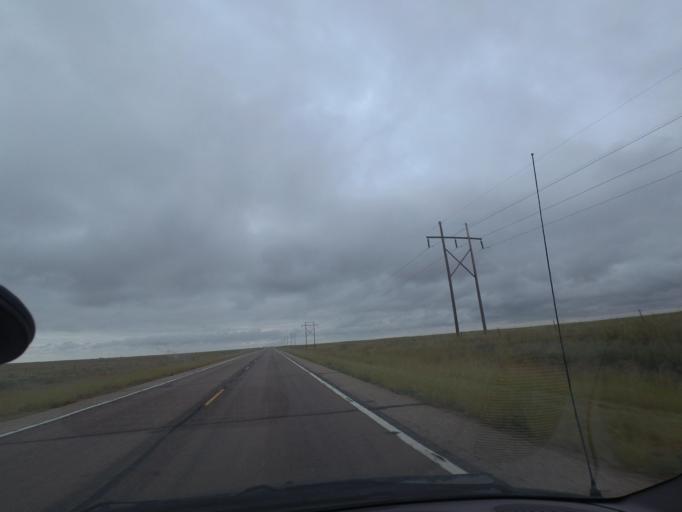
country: US
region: Colorado
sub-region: Yuma County
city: Yuma
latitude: 39.6549
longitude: -102.8097
